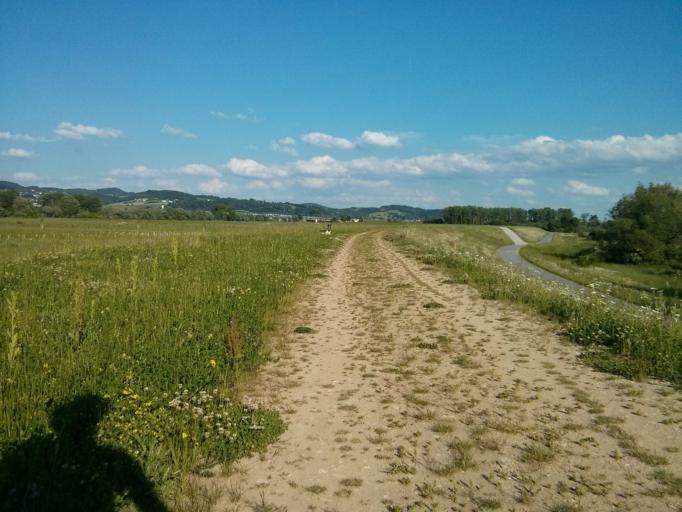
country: DE
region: Bavaria
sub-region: Lower Bavaria
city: Metten
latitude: 48.8325
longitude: 12.9256
